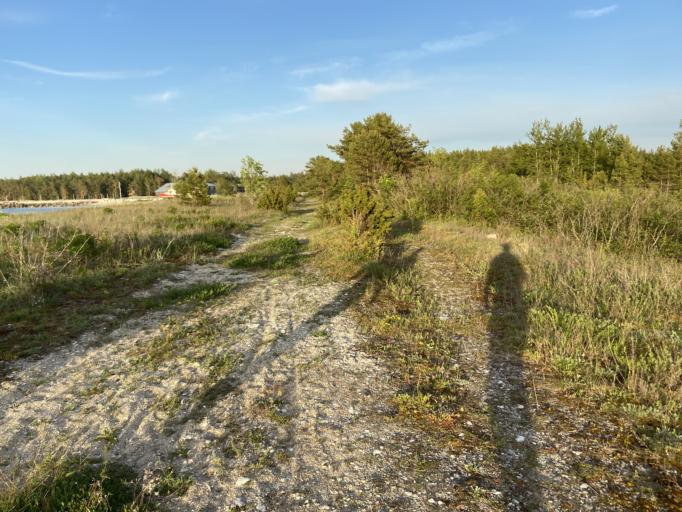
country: EE
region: Harju
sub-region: Paldiski linn
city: Paldiski
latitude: 59.2700
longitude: 23.7402
